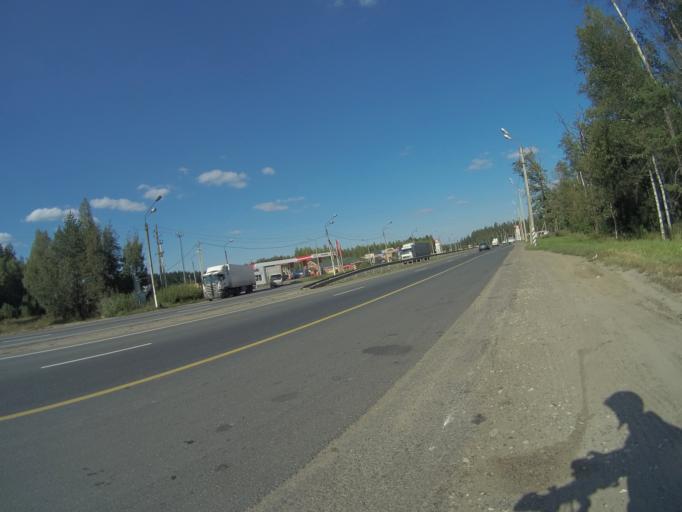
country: RU
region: Vladimir
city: Kommunar
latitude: 56.0611
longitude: 40.4535
